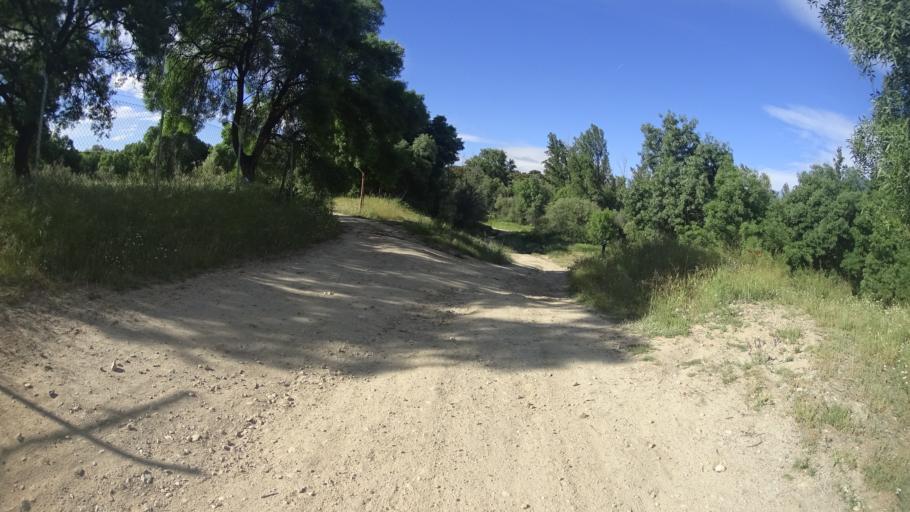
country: ES
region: Madrid
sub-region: Provincia de Madrid
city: Villanueva del Pardillo
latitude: 40.5090
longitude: -3.9398
